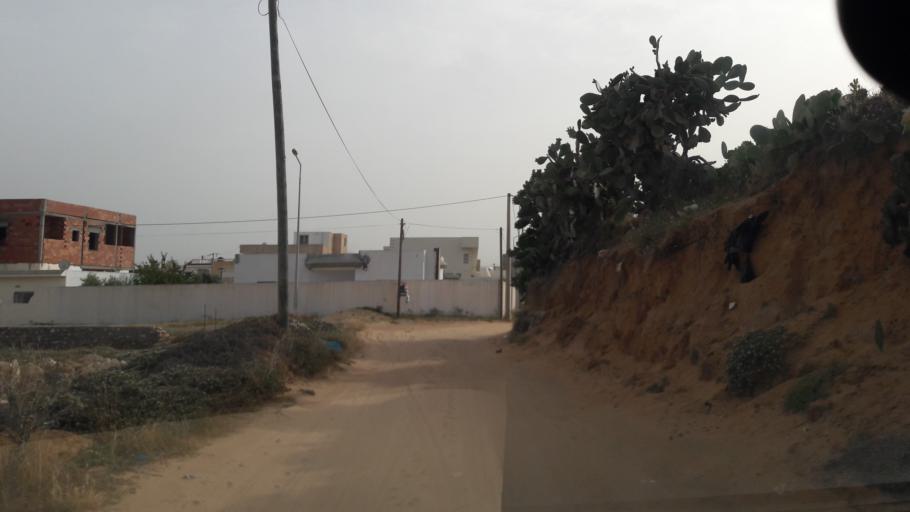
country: TN
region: Safaqis
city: Al Qarmadah
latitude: 34.7805
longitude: 10.7735
